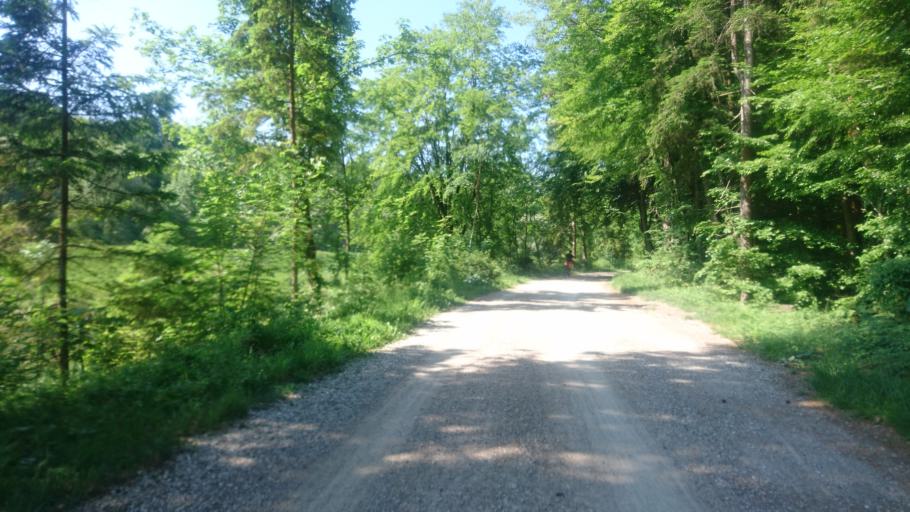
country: DE
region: Bavaria
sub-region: Upper Bavaria
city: Pullach im Isartal
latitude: 48.0591
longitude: 11.5373
